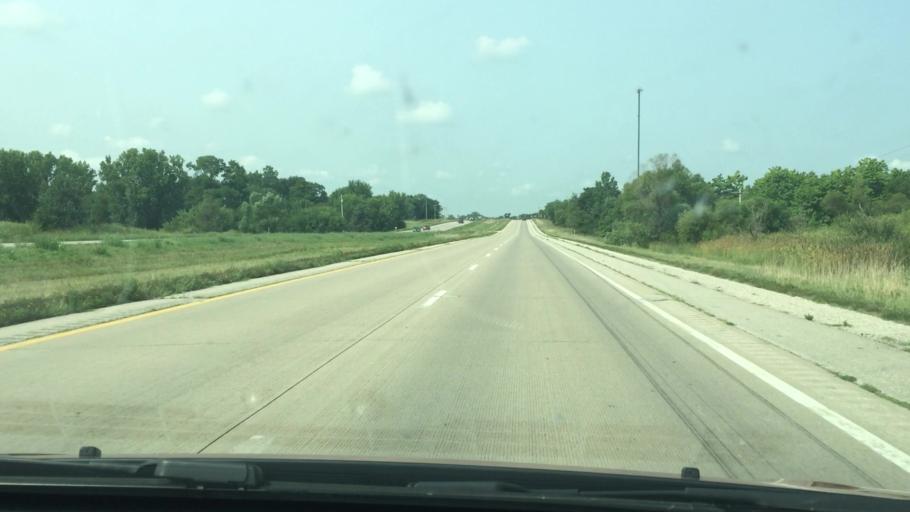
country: US
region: Iowa
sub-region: Cedar County
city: Durant
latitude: 41.5185
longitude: -90.8919
